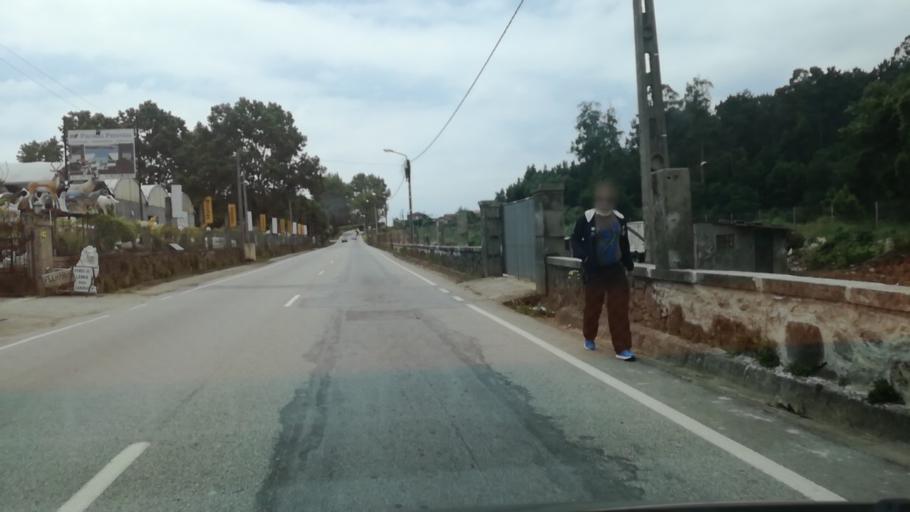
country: PT
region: Porto
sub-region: Maia
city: Anta
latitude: 41.2903
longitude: -8.6013
